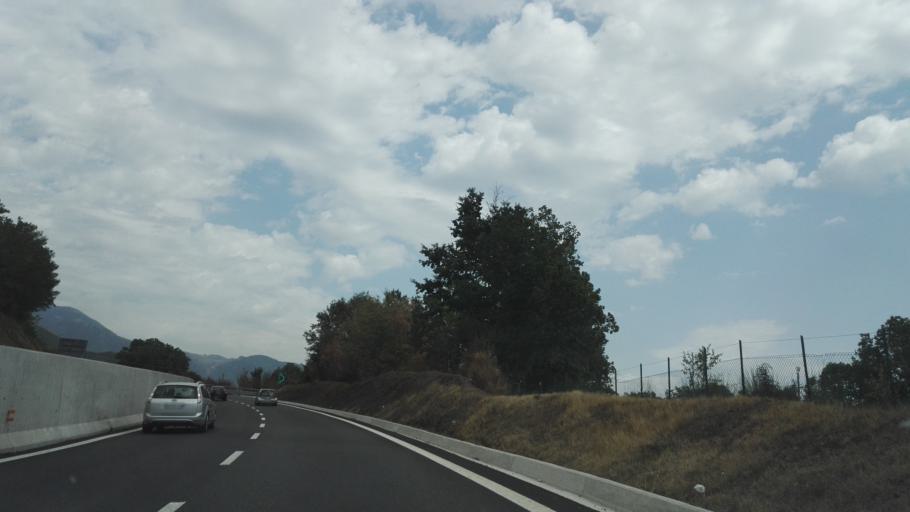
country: IT
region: Calabria
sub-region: Provincia di Cosenza
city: Laino Borgo
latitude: 39.9723
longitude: 15.9359
